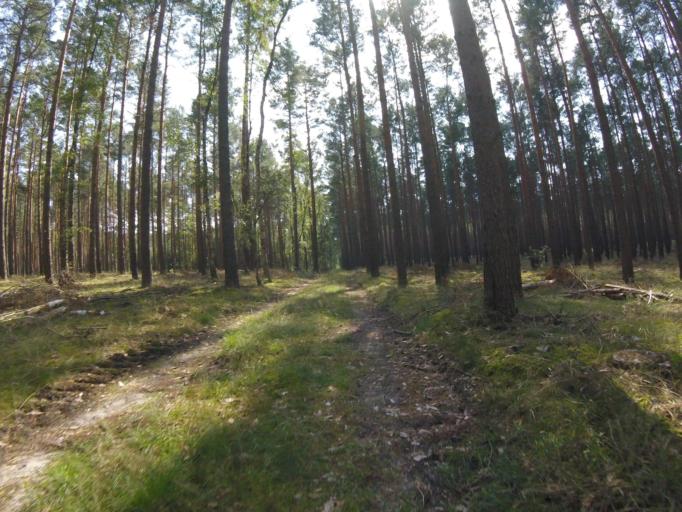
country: DE
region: Brandenburg
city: Gross Koris
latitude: 52.2097
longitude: 13.6955
